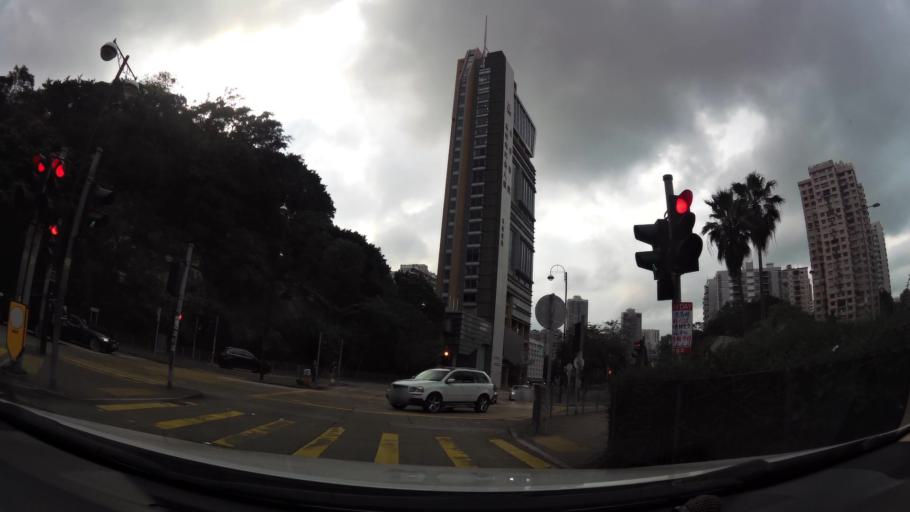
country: HK
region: Kowloon City
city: Kowloon
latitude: 22.3119
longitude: 114.1767
